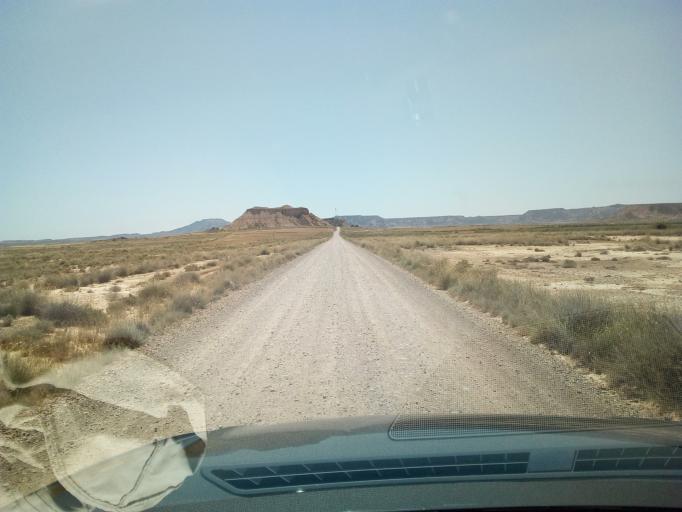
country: ES
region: Navarre
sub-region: Provincia de Navarra
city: Arguedas
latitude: 42.1995
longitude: -1.4958
